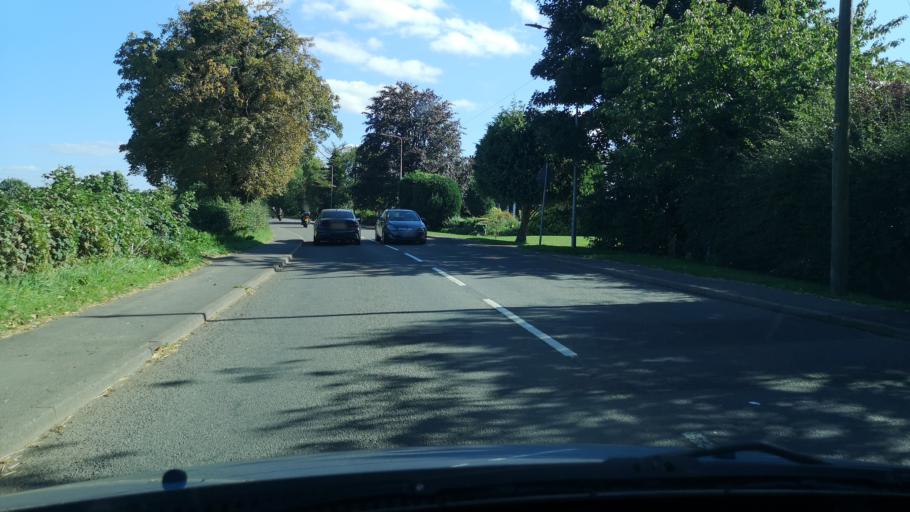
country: GB
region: England
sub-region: North Lincolnshire
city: Crowle
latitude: 53.5992
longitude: -0.8264
